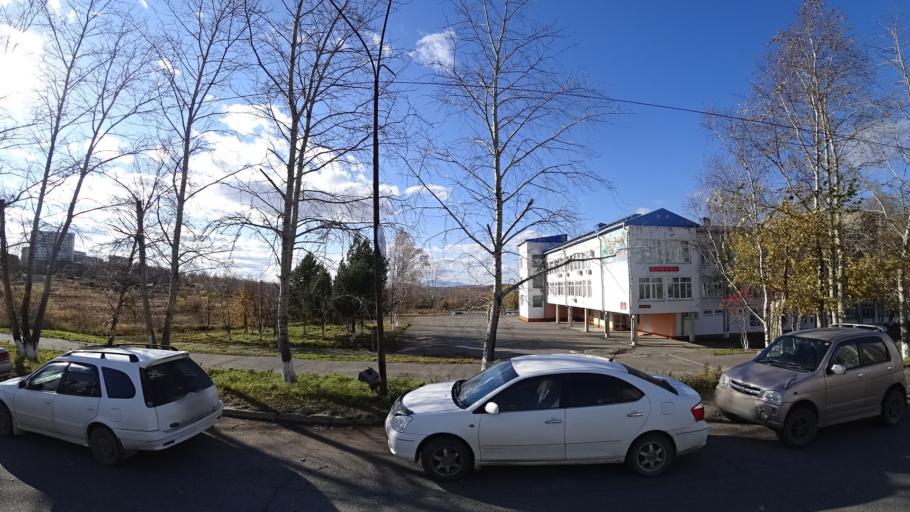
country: RU
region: Khabarovsk Krai
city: Amursk
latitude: 50.2469
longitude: 136.9162
